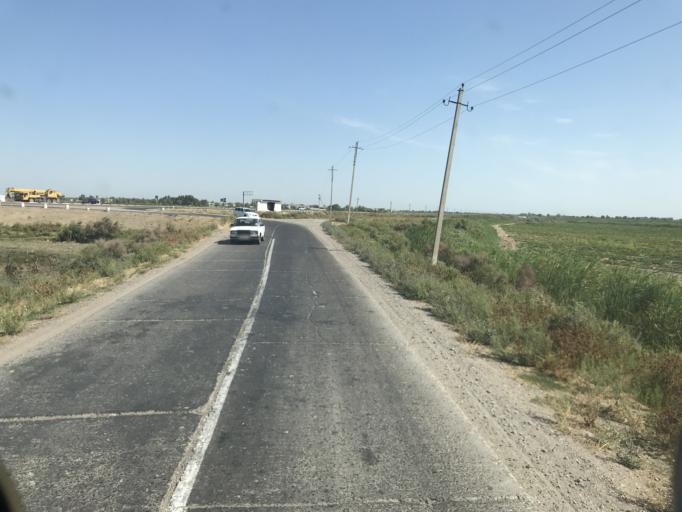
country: KZ
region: Ongtustik Qazaqstan
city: Myrzakent
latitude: 40.7477
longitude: 68.5375
